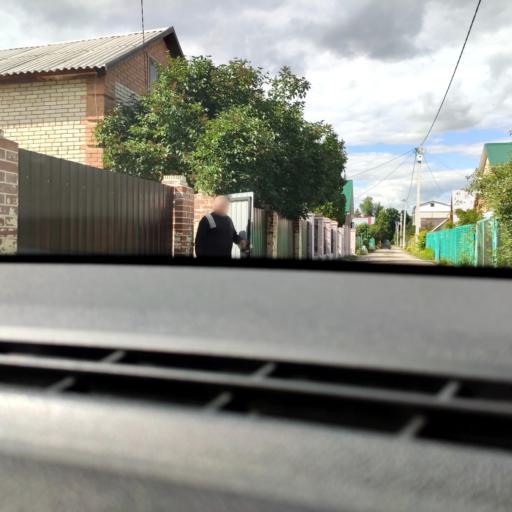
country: RU
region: Samara
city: Podstepki
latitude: 53.5827
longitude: 49.0740
